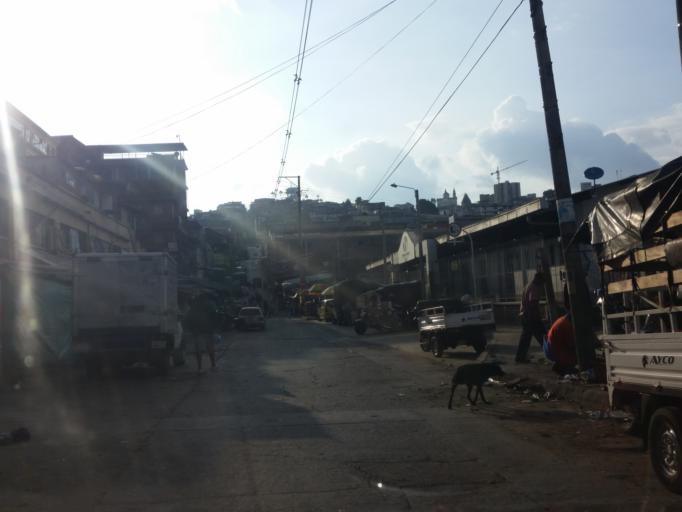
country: CO
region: Caldas
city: Manizales
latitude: 5.0724
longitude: -75.5166
